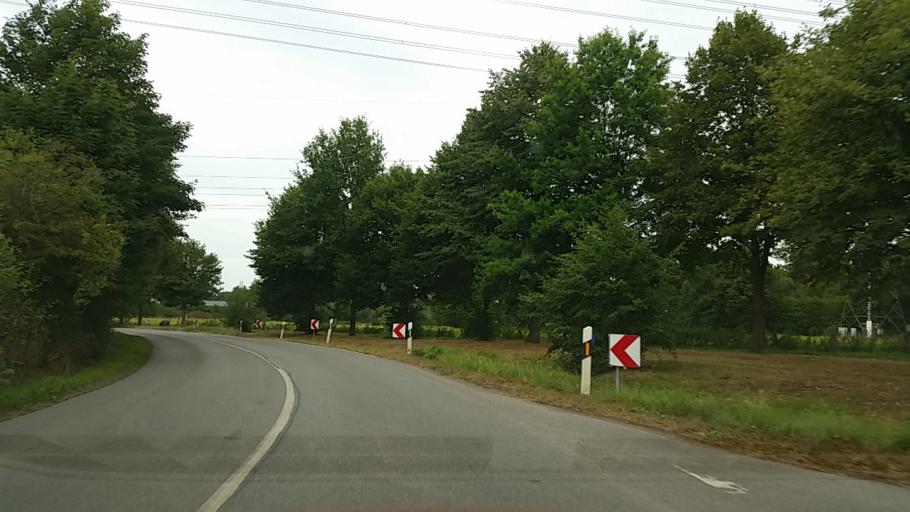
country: DE
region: Schleswig-Holstein
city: Bonningstedt
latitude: 53.6929
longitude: 9.9379
